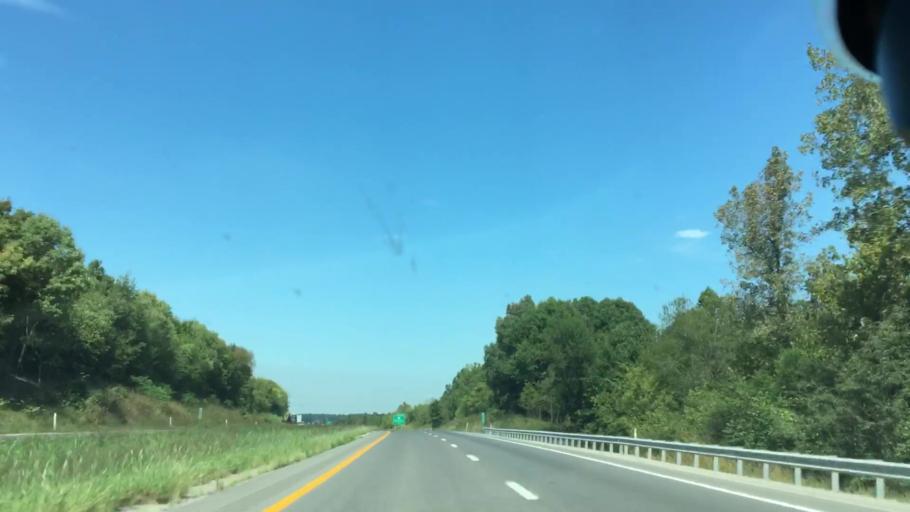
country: US
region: Kentucky
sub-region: Hopkins County
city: Earlington
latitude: 37.2816
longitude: -87.4567
